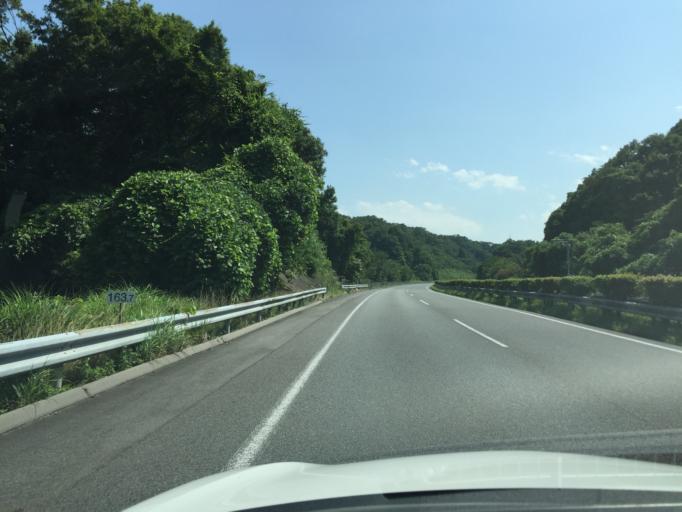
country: JP
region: Fukushima
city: Iwaki
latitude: 36.9749
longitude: 140.7943
